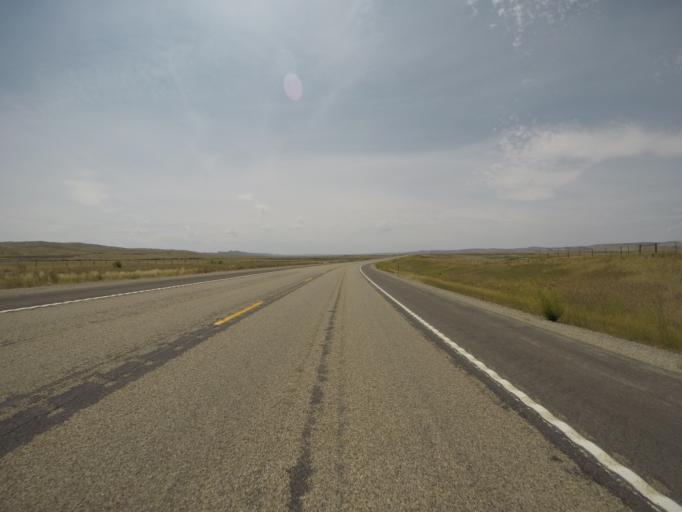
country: US
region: Wyoming
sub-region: Lincoln County
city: Kemmerer
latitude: 41.7378
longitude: -110.5633
